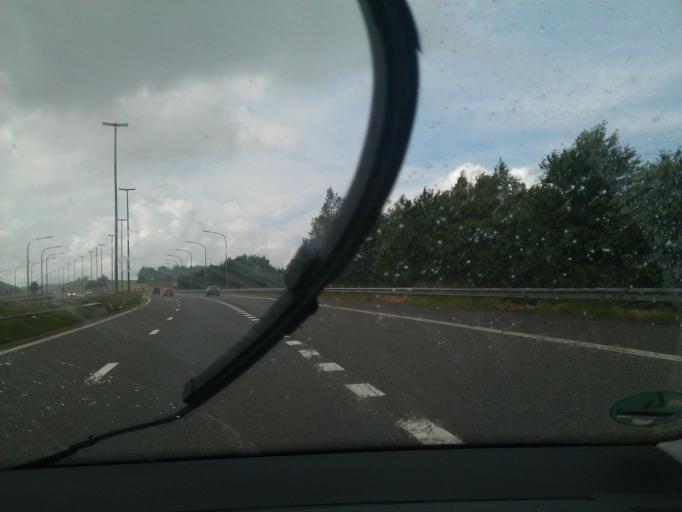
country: BE
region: Wallonia
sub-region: Province de Liege
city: Saint-Vith
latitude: 50.2860
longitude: 6.1052
